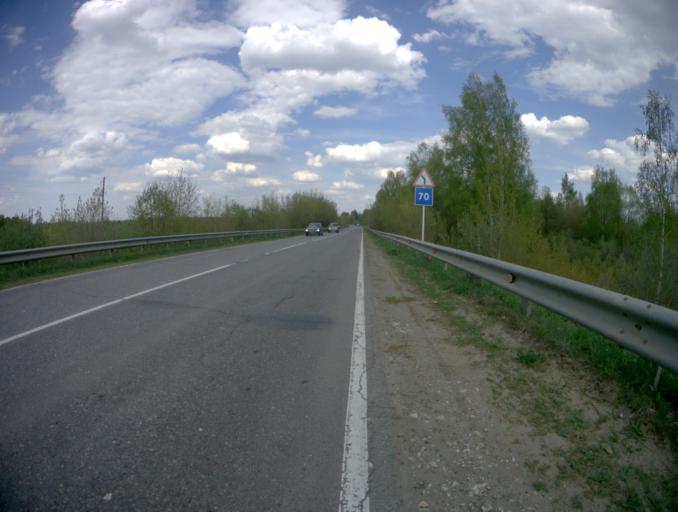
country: RU
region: Vladimir
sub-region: Kovrovskiy Rayon
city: Kovrov
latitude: 56.4349
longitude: 41.2567
